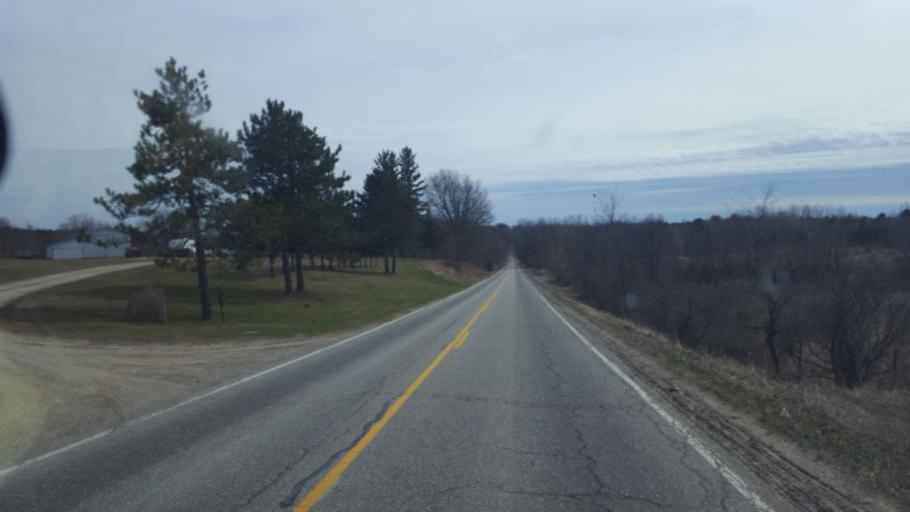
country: US
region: Michigan
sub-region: Isabella County
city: Lake Isabella
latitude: 43.5633
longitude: -85.0262
